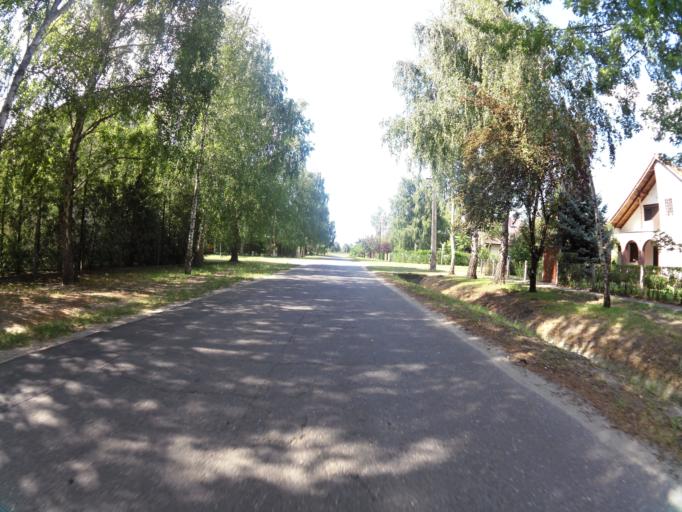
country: HU
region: Csongrad
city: Sandorfalva
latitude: 46.3637
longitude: 20.1061
